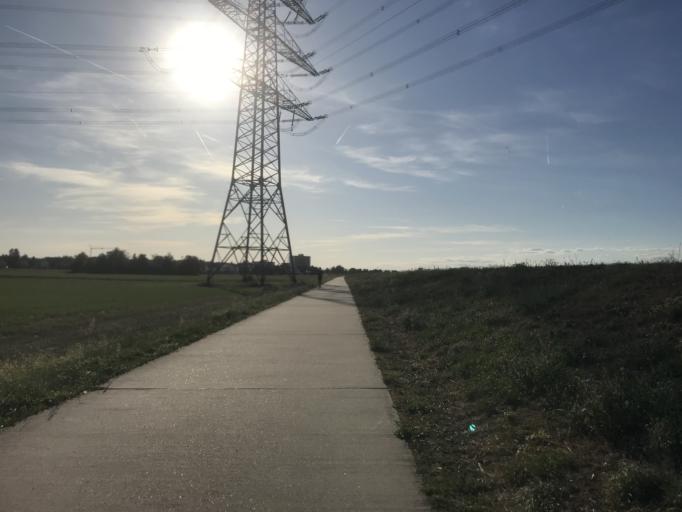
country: DE
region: Hesse
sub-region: Regierungsbezirk Darmstadt
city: Bischofsheim
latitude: 49.9964
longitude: 8.3734
